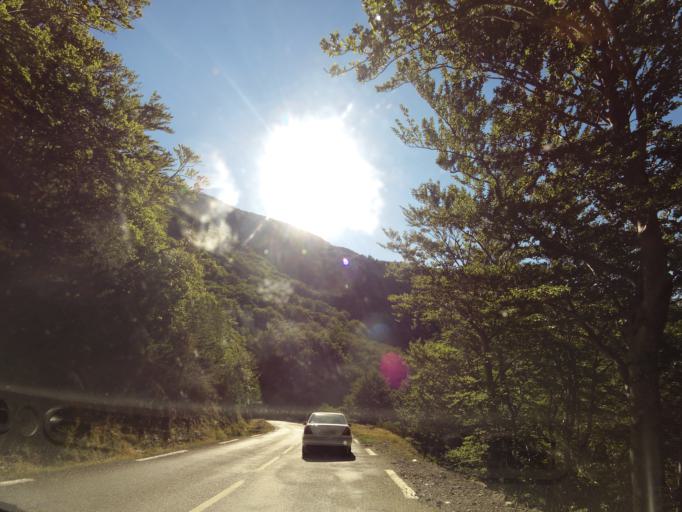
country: FR
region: Languedoc-Roussillon
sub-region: Departement du Gard
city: Valleraugue
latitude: 44.0866
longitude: 3.5798
